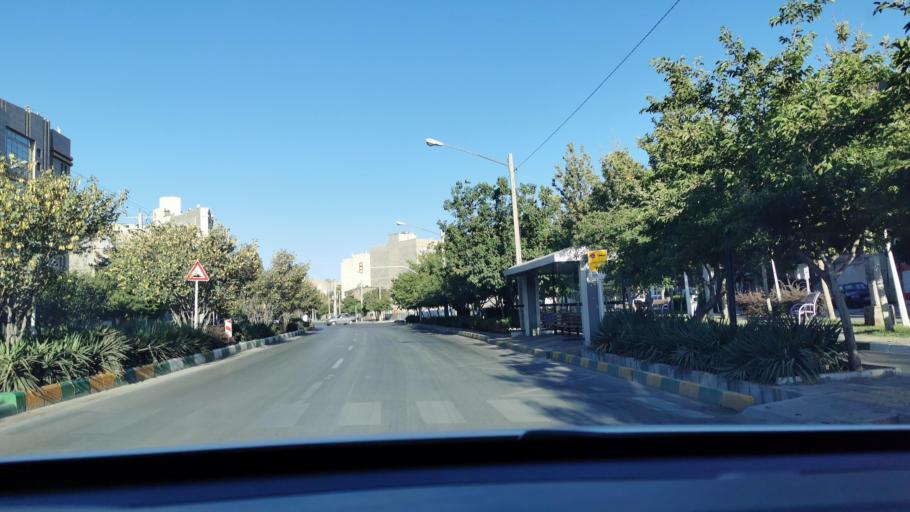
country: IR
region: Razavi Khorasan
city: Mashhad
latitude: 36.3519
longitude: 59.4828
